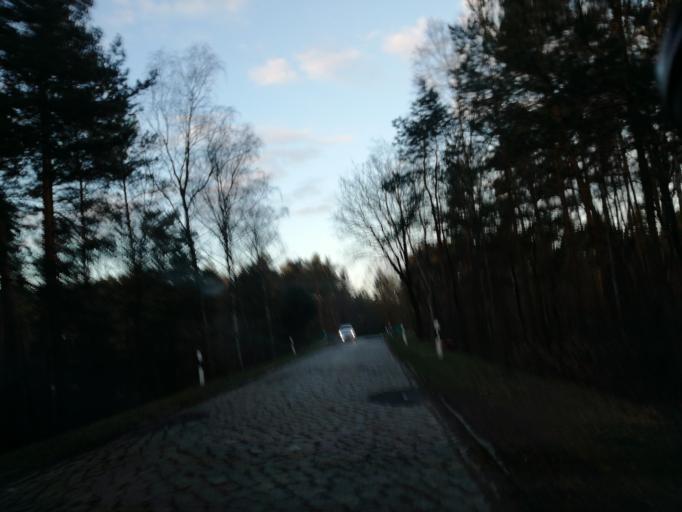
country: DE
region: Brandenburg
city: Bronkow
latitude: 51.7221
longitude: 13.8847
